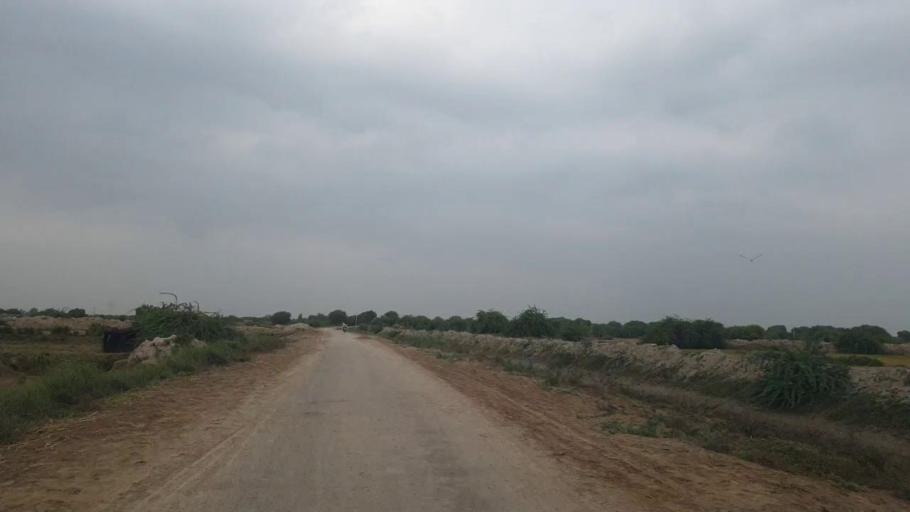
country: PK
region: Sindh
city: Badin
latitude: 24.6282
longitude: 68.6818
